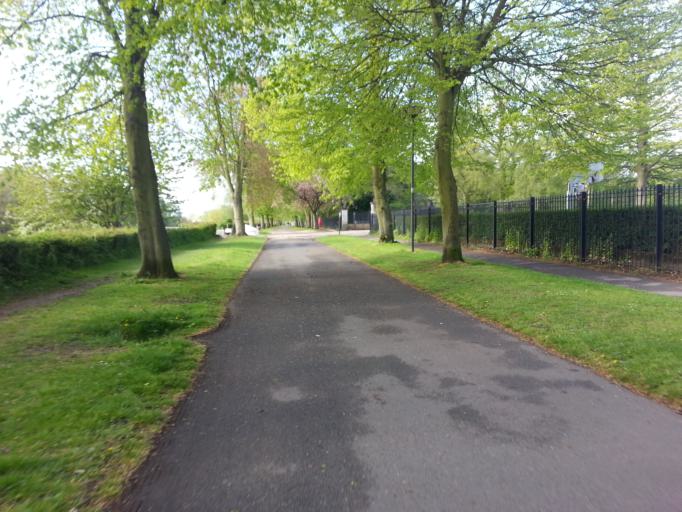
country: GB
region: England
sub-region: City of York
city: York
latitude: 53.9487
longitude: -1.0797
